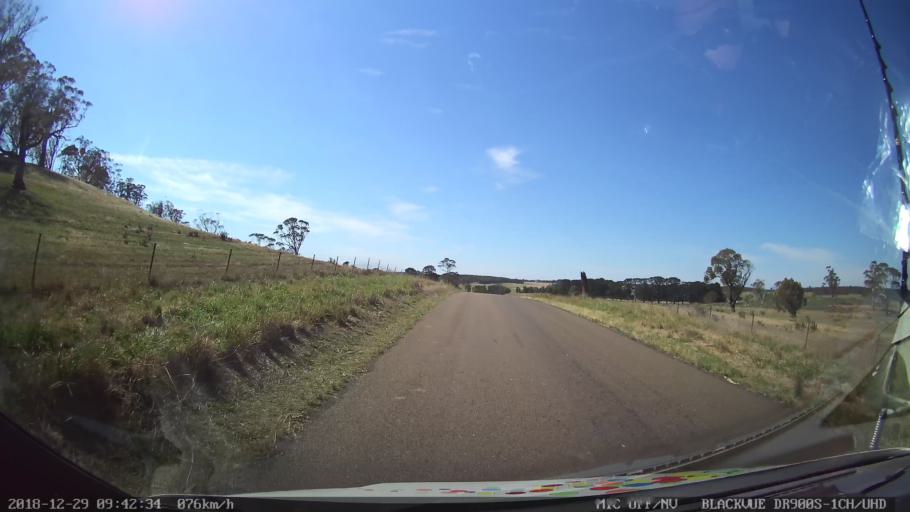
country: AU
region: New South Wales
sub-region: Upper Lachlan Shire
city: Crookwell
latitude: -34.6711
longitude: 149.4211
